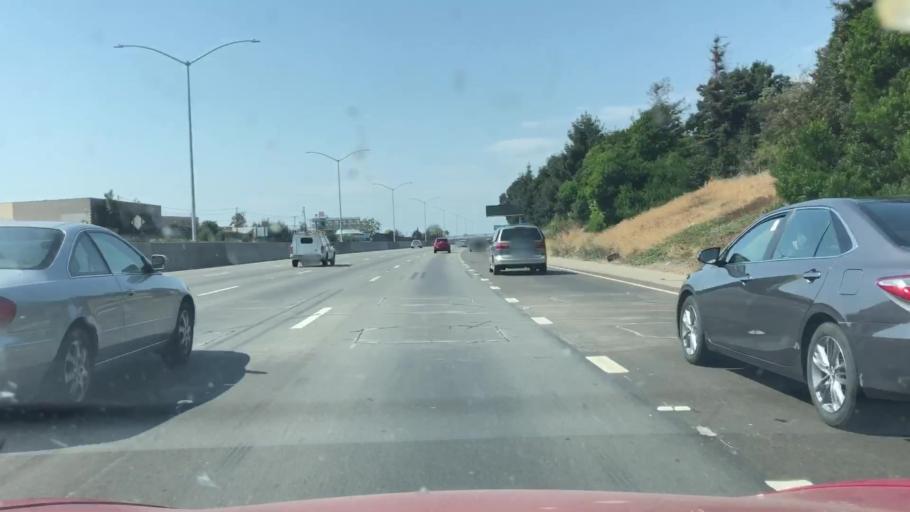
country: US
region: California
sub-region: Alameda County
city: San Leandro
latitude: 37.7123
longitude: -122.1725
